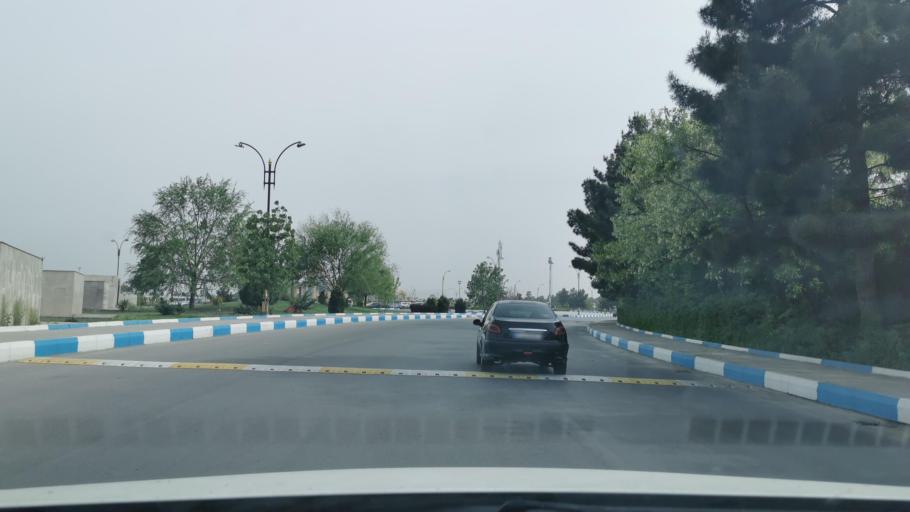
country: IR
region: Razavi Khorasan
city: Mashhad
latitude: 36.2286
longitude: 59.6388
